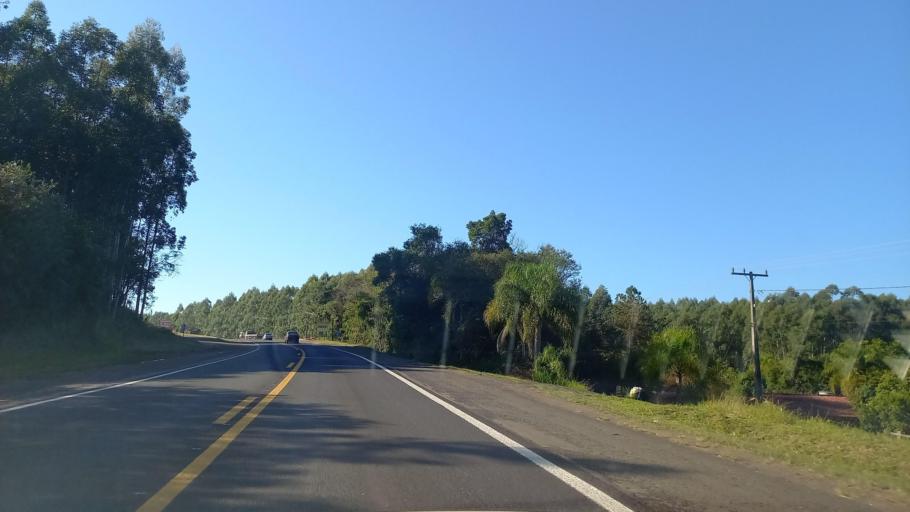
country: BR
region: Rio Grande do Sul
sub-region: Taquari
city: Taquari
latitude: -29.7112
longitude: -51.7775
